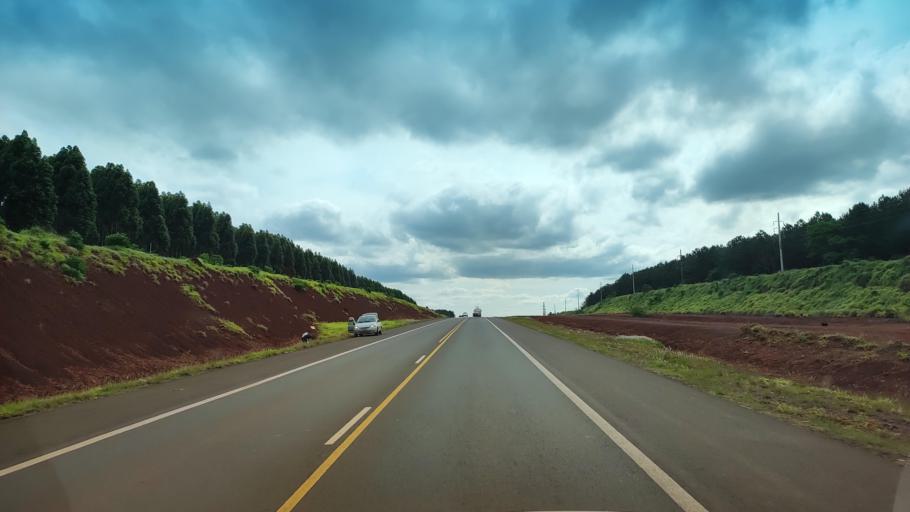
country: AR
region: Misiones
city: Garupa
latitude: -27.4654
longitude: -55.9046
